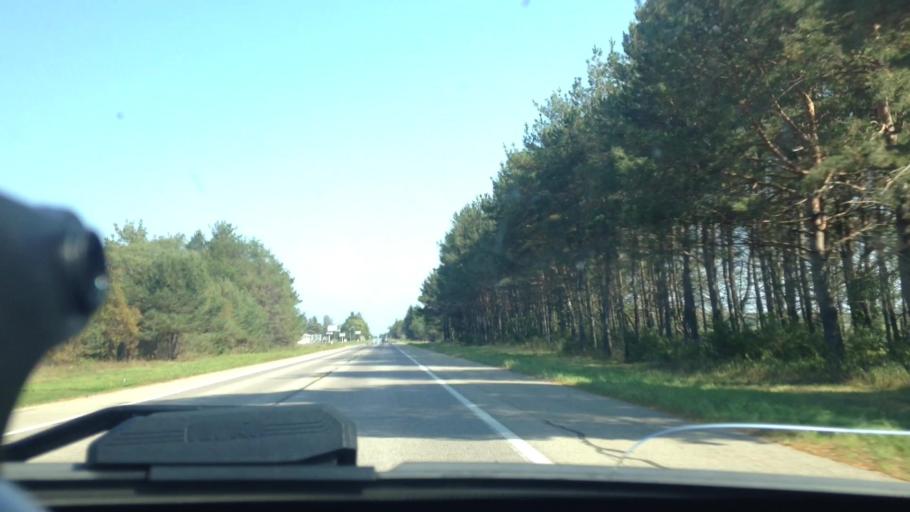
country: US
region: Michigan
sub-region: Luce County
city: Newberry
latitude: 46.3034
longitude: -85.4760
